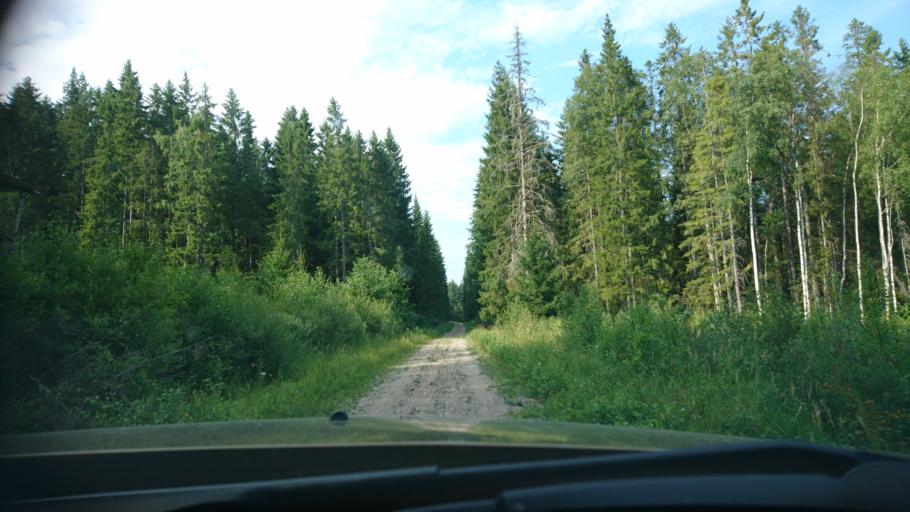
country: SE
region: Vaermland
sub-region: Kristinehamns Kommun
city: Bjorneborg
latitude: 59.2992
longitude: 14.3078
